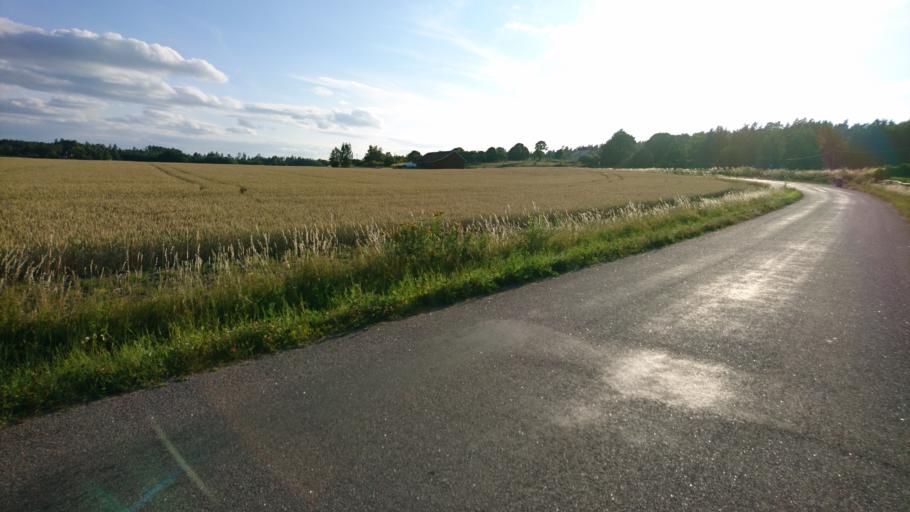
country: SE
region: Soedermanland
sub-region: Strangnas Kommun
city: Stallarholmen
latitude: 59.4024
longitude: 17.2788
